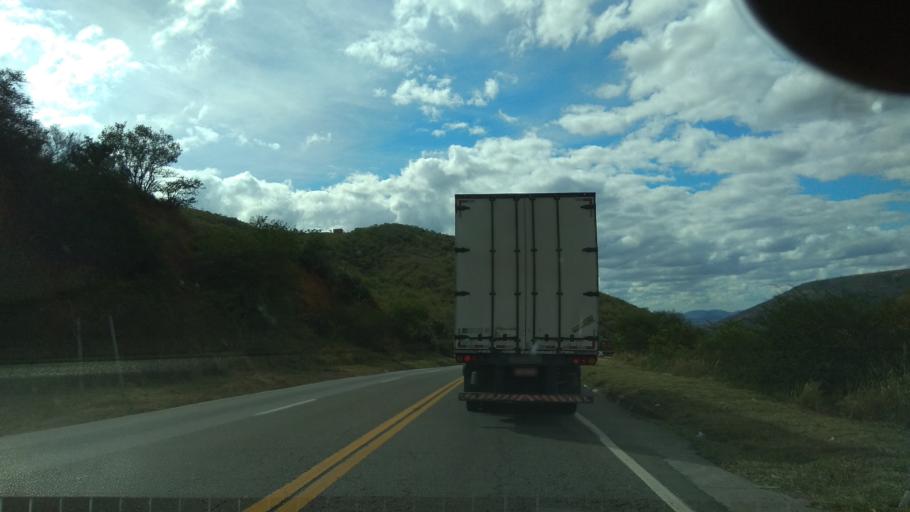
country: BR
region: Bahia
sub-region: Amargosa
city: Amargosa
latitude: -12.8987
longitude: -39.8616
